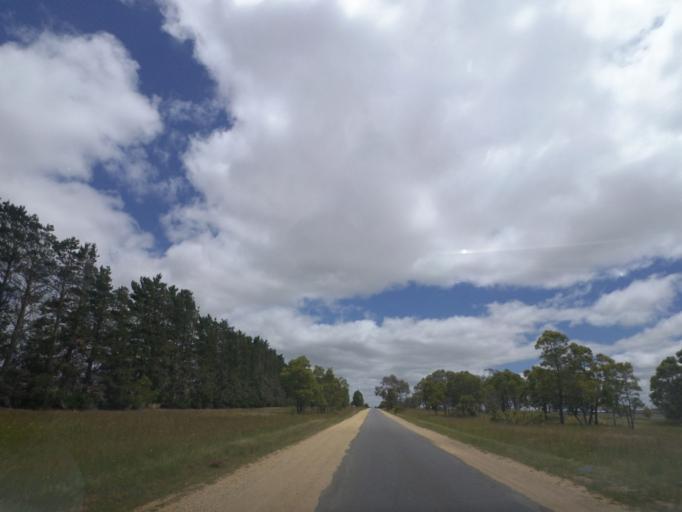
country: AU
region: Victoria
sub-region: Moorabool
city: Bacchus Marsh
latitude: -37.6145
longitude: 144.2475
